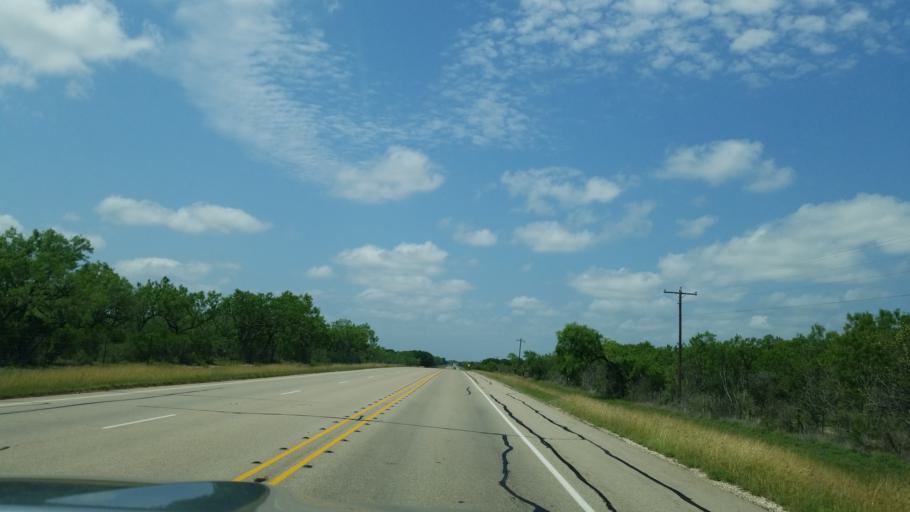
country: US
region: Texas
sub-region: Frio County
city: Pearsall
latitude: 29.0035
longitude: -99.2151
